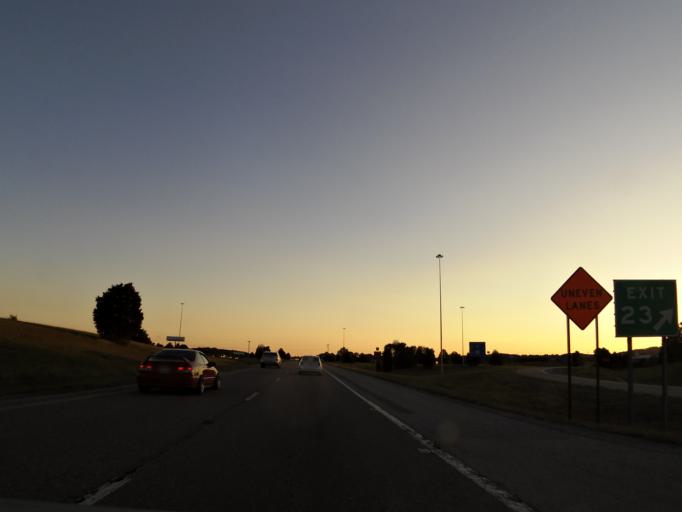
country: US
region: Tennessee
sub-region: Greene County
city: Mosheim
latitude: 36.2255
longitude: -83.0378
